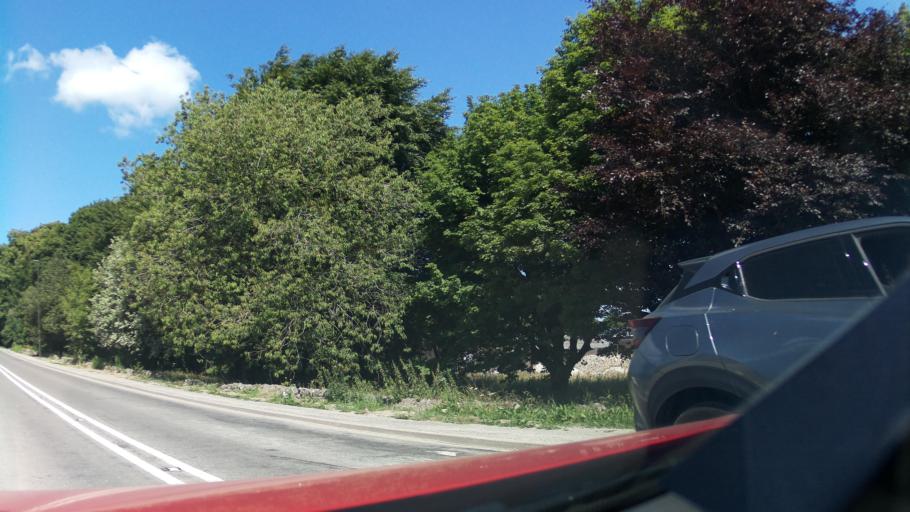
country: GB
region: England
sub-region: Derbyshire
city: Buxton
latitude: 53.2430
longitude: -1.8990
